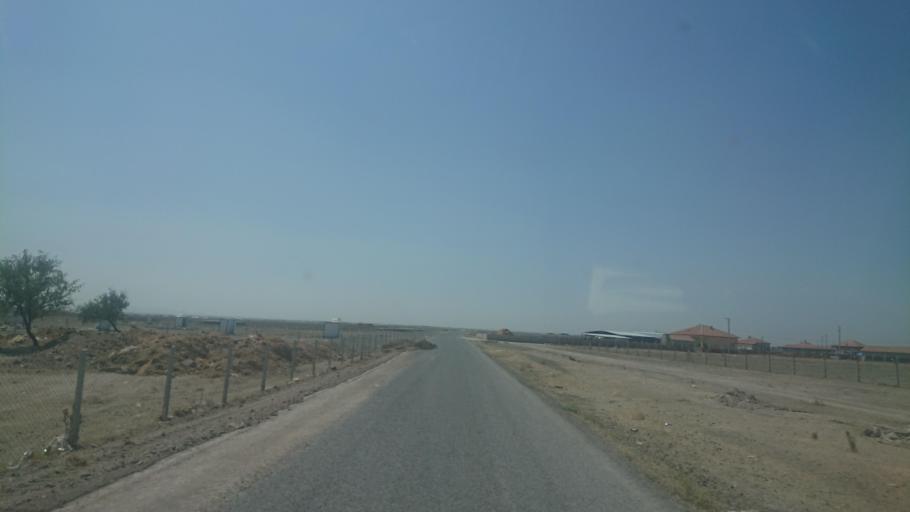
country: TR
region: Aksaray
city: Yesilova
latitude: 38.3319
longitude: 33.7501
